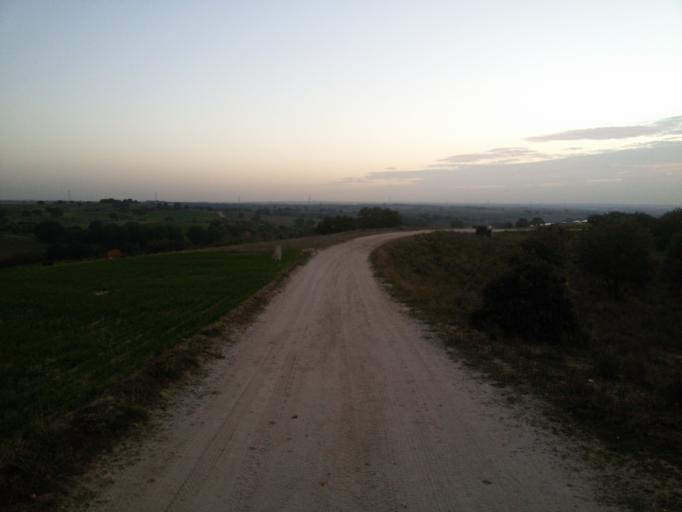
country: ES
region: Madrid
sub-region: Provincia de Madrid
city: Sevilla La Nueva
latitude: 40.3316
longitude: -4.0262
